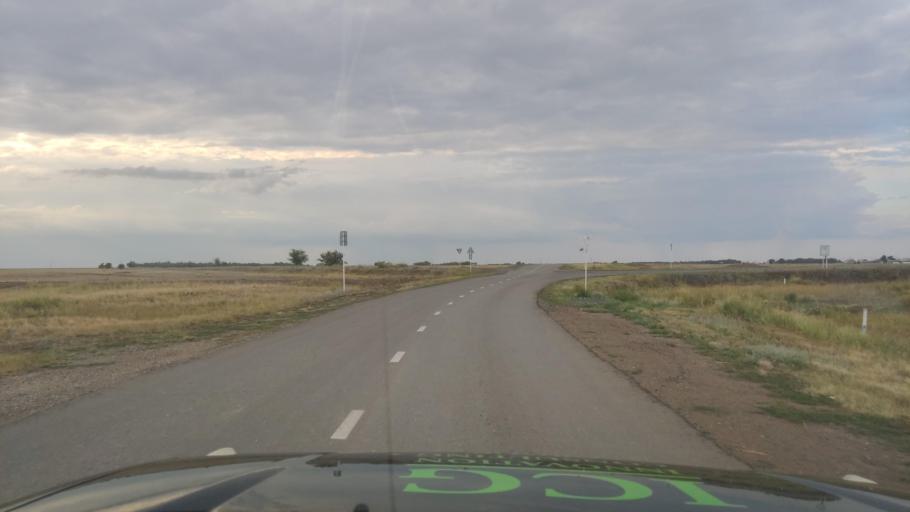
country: KZ
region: Pavlodar
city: Pavlodar
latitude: 52.3463
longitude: 77.2534
